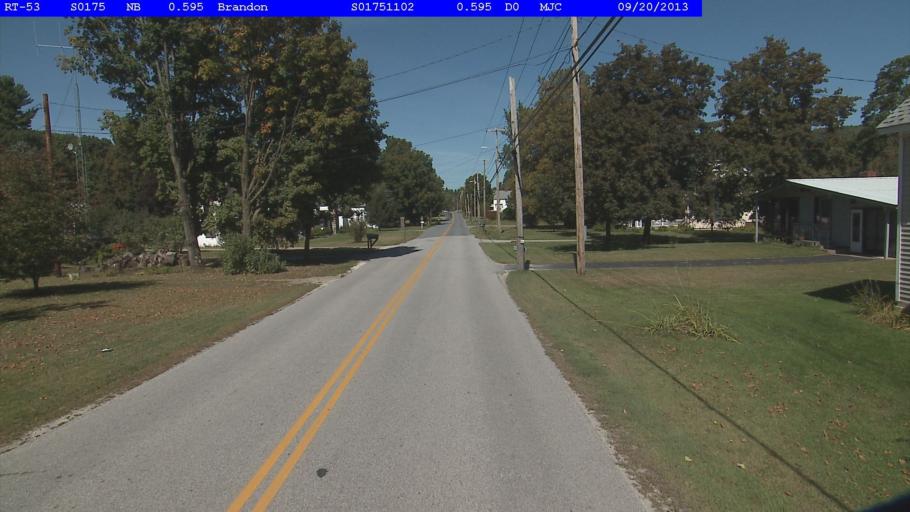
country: US
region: Vermont
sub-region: Rutland County
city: Brandon
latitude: 43.8353
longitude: -73.0557
